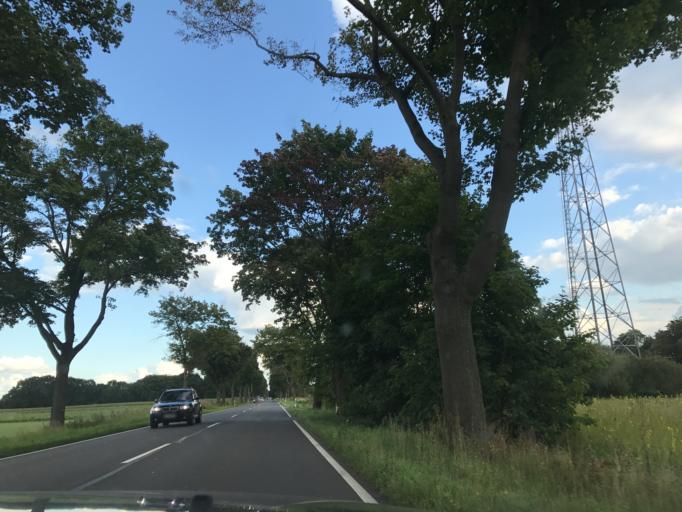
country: DE
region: Lower Saxony
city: Klein Schwulper
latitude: 52.3302
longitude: 10.4302
